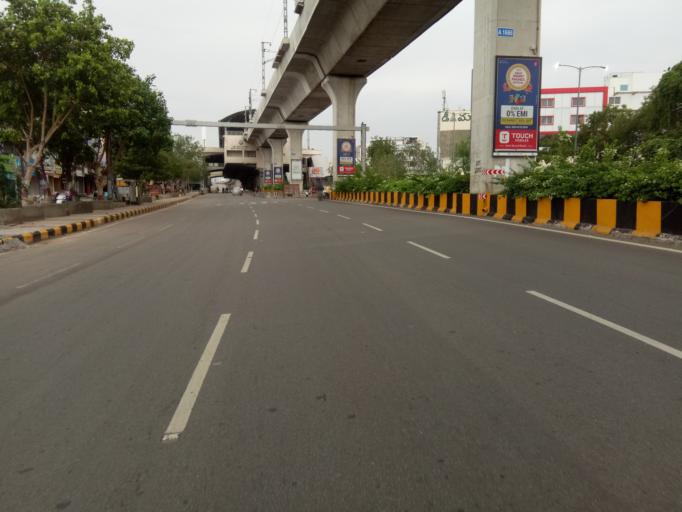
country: IN
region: Telangana
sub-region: Rangareddi
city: Lal Bahadur Nagar
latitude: 17.3514
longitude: 78.5474
